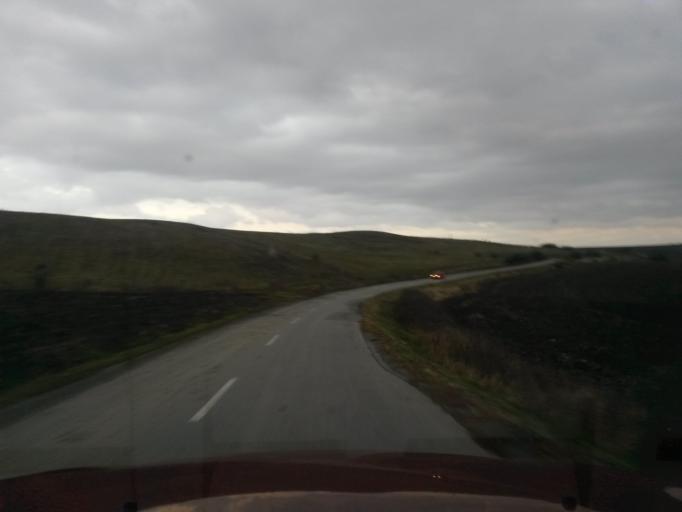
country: SK
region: Kosicky
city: Kosice
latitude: 48.8057
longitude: 21.2655
